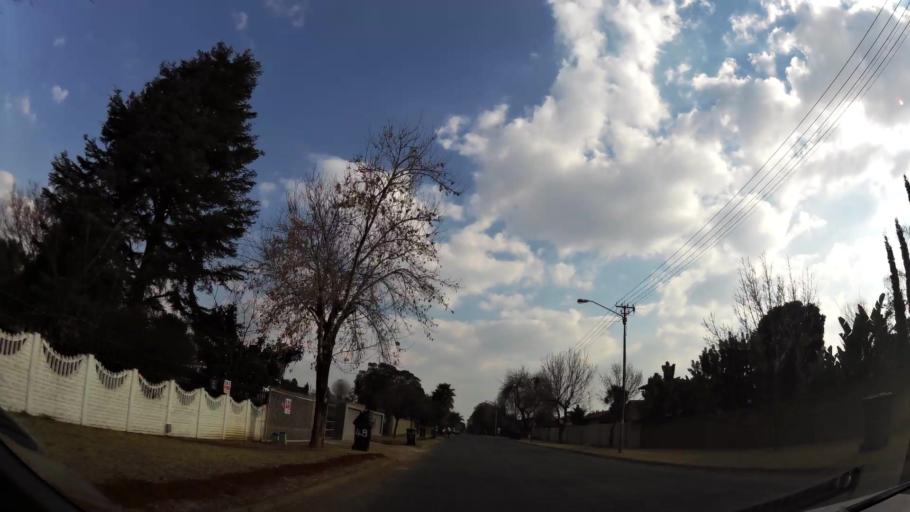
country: ZA
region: Gauteng
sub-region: Ekurhuleni Metropolitan Municipality
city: Germiston
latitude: -26.2506
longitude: 28.1777
